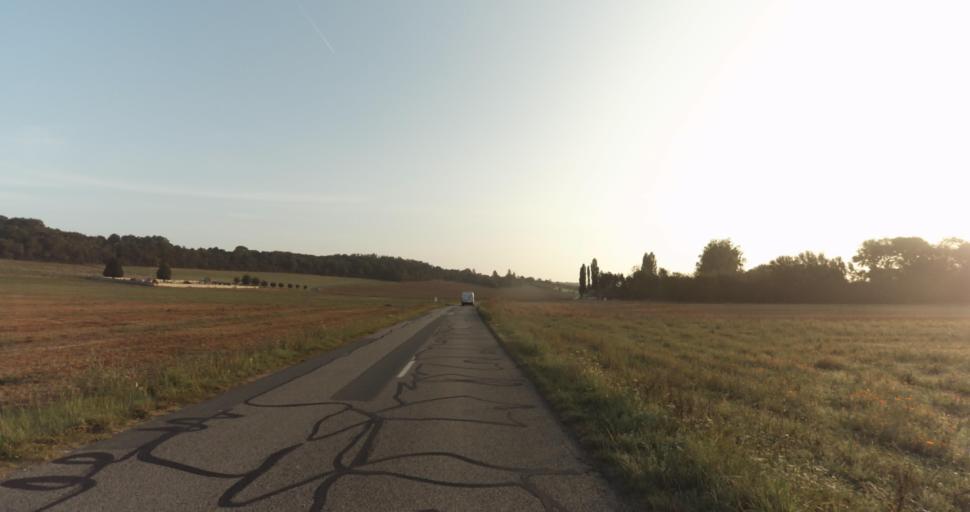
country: FR
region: Centre
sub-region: Departement d'Eure-et-Loir
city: Vert-en-Drouais
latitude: 48.7777
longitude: 1.3387
